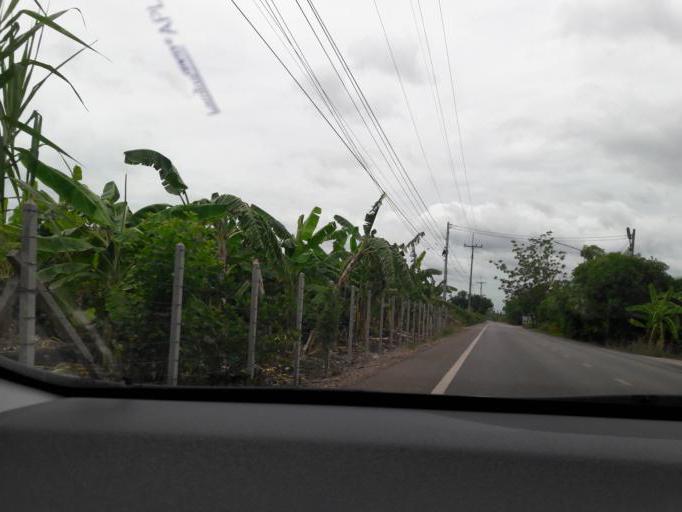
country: TH
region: Ratchaburi
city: Damnoen Saduak
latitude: 13.5624
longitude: 100.0130
